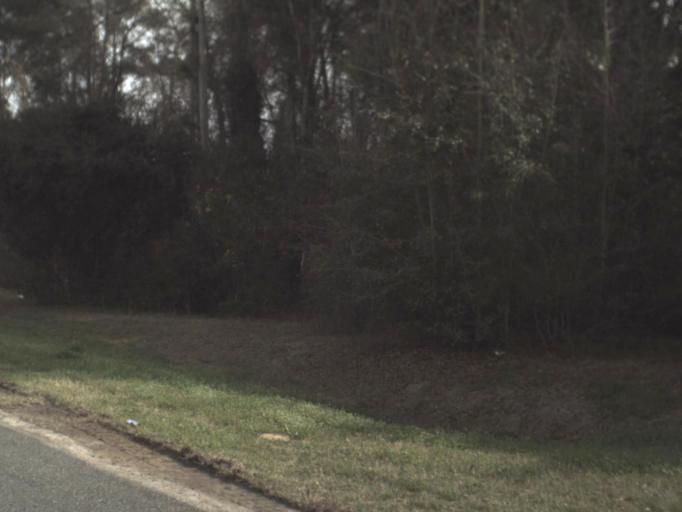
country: US
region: Florida
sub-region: Jefferson County
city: Monticello
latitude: 30.5142
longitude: -83.7789
